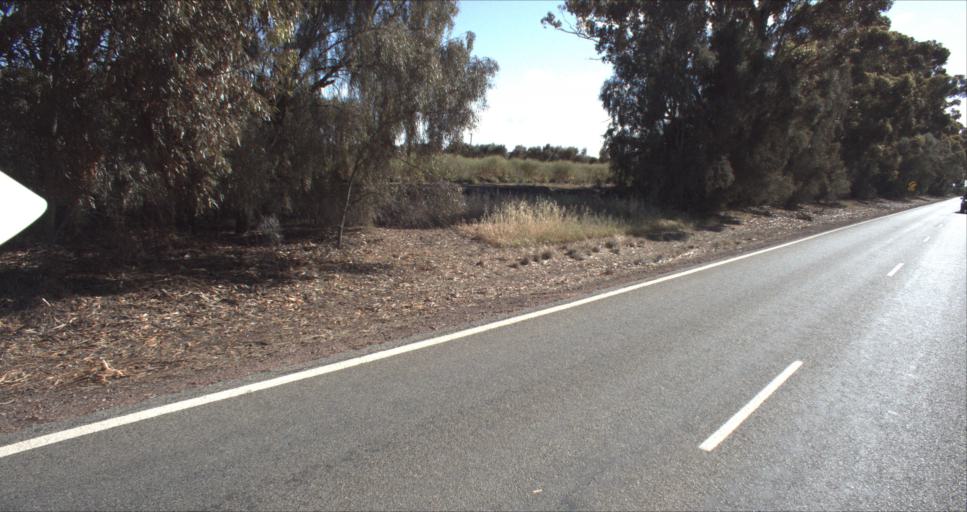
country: AU
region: New South Wales
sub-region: Leeton
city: Leeton
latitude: -34.5447
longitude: 146.3298
